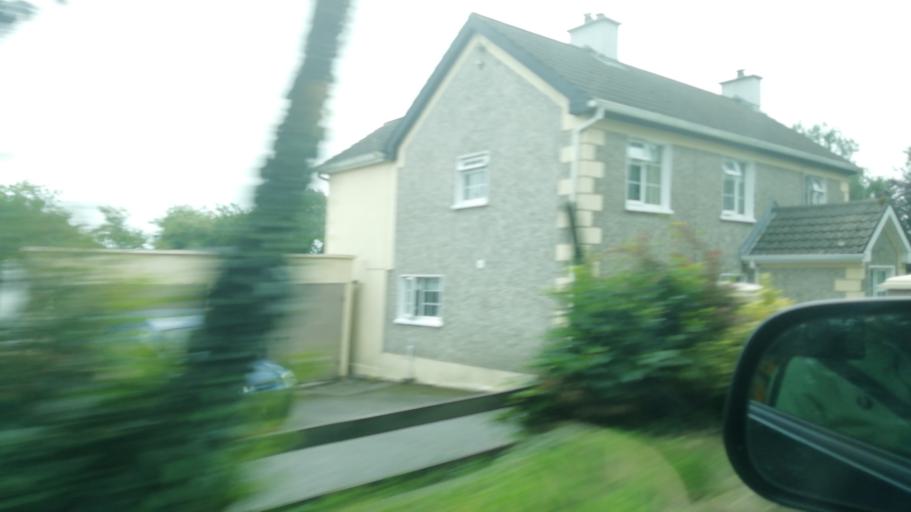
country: IE
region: Munster
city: Fethard
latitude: 52.5555
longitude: -7.6702
